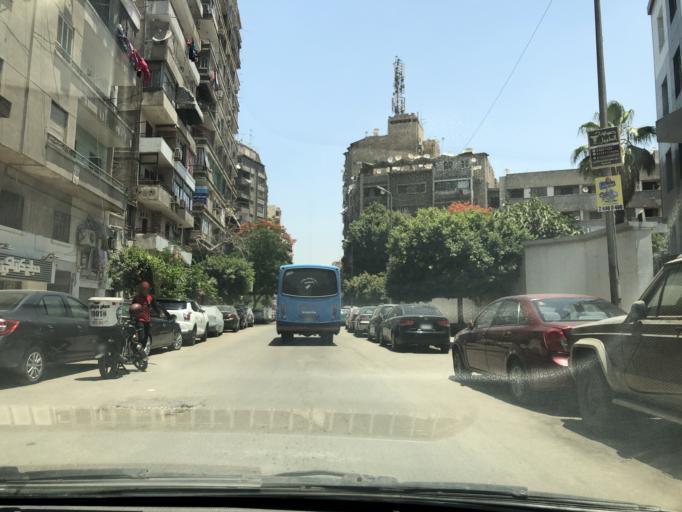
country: EG
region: Muhafazat al Qahirah
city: Cairo
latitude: 30.0630
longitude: 31.2743
